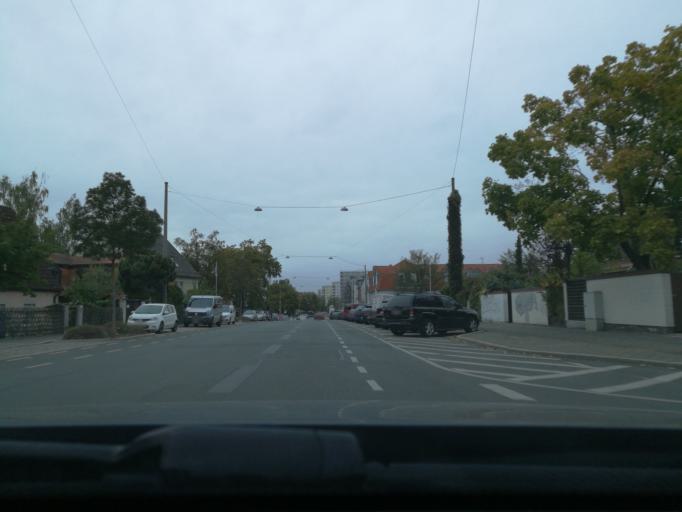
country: DE
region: Bavaria
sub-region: Regierungsbezirk Mittelfranken
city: Furth
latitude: 49.4784
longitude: 11.0027
